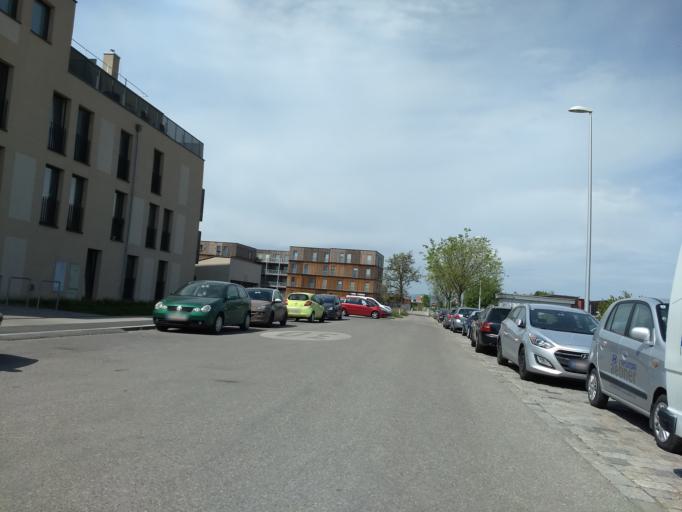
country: AT
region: Lower Austria
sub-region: Politischer Bezirk Ganserndorf
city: Aderklaa
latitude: 48.2411
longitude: 16.4969
